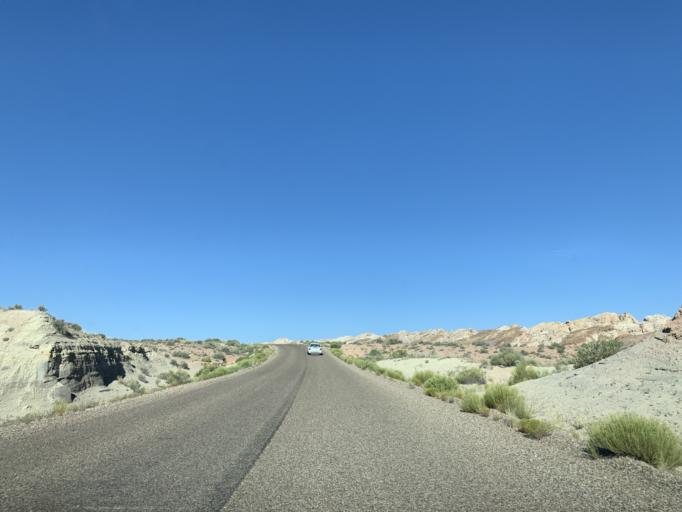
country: US
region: Utah
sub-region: Emery County
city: Ferron
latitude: 38.5818
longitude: -110.7916
